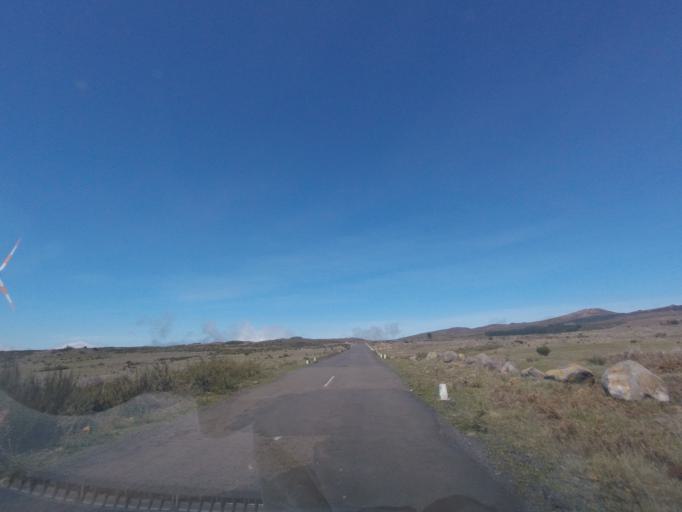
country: PT
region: Madeira
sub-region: Calheta
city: Arco da Calheta
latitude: 32.7441
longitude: -17.0974
